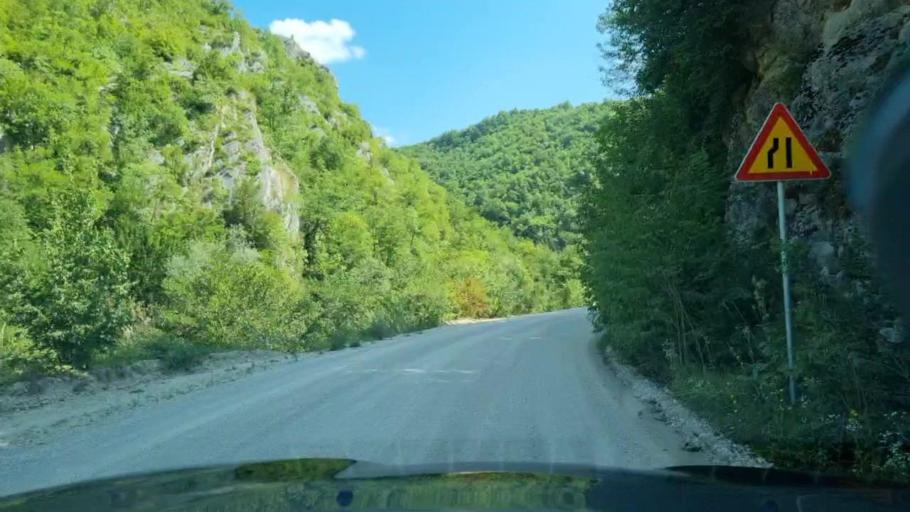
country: BA
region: Federation of Bosnia and Herzegovina
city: Kljuc
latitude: 44.5549
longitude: 16.8249
